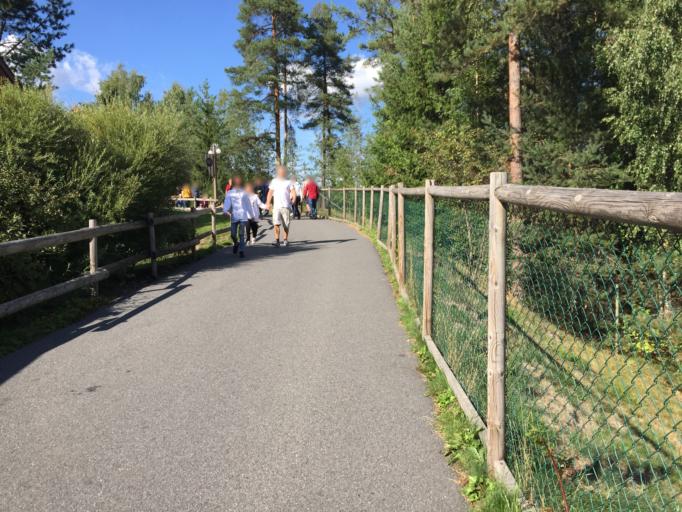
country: NO
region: Akershus
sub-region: Ski
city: Ski
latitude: 59.7460
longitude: 10.7776
